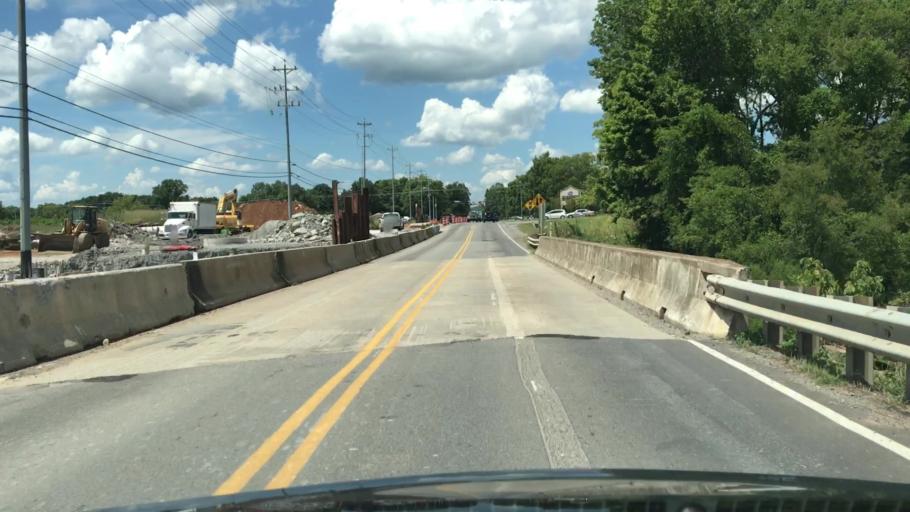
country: US
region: Tennessee
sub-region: Rutherford County
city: Murfreesboro
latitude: 35.8434
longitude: -86.4898
